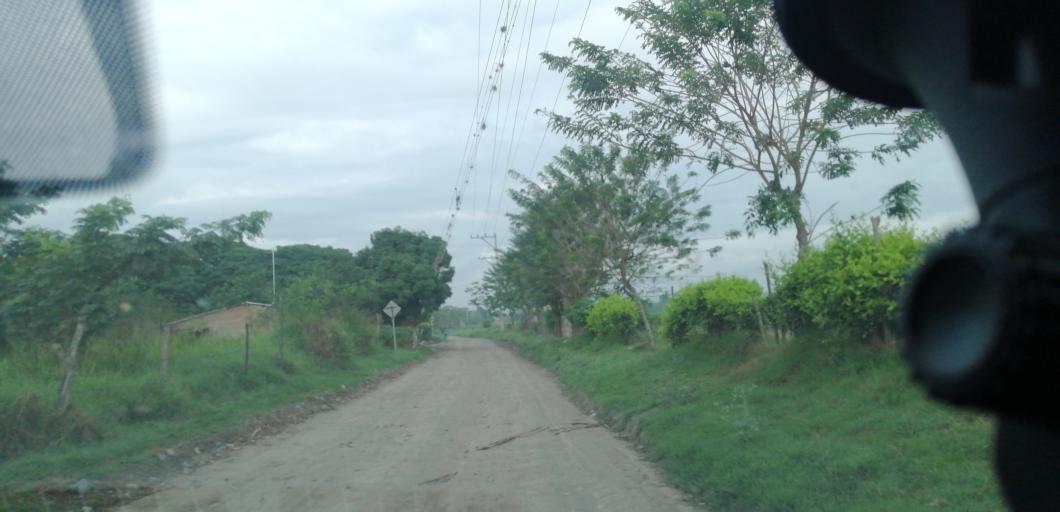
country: CO
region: Valle del Cauca
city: Yumbo
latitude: 3.5715
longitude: -76.3977
